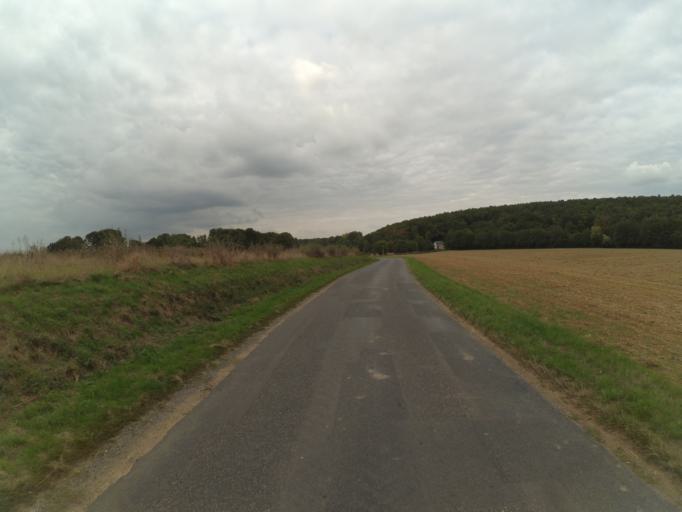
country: FR
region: Centre
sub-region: Departement d'Indre-et-Loire
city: Poce-sur-Cisse
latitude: 47.4846
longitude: 0.9829
